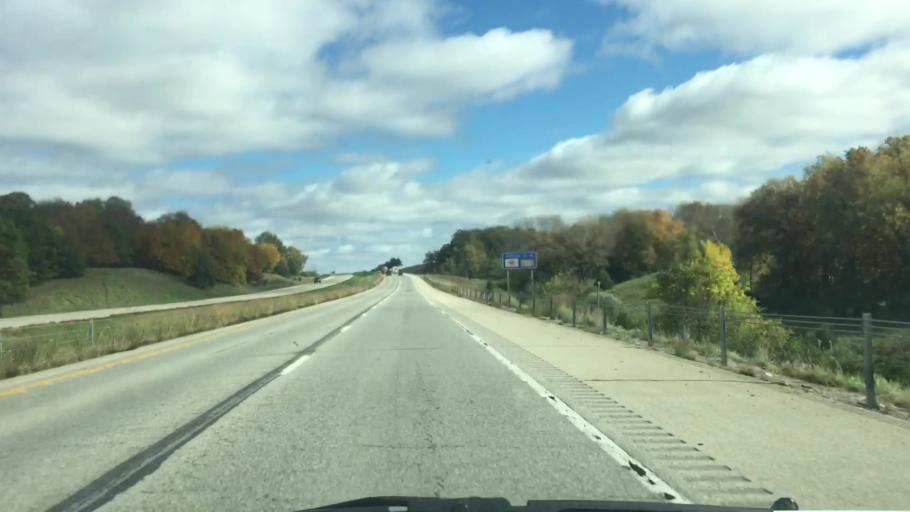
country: US
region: Iowa
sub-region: Poweshiek County
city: Grinnell
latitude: 41.6951
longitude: -92.7514
